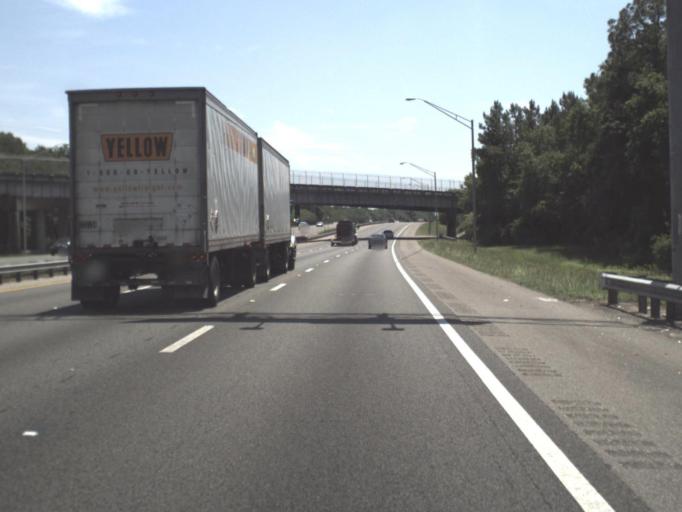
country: US
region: Florida
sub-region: Clay County
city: Bellair-Meadowbrook Terrace
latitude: 30.2594
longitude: -81.7638
